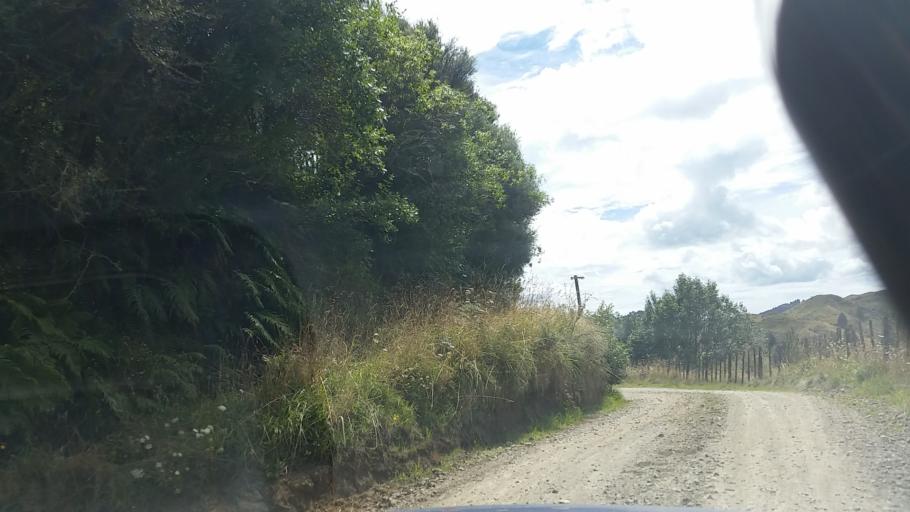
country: NZ
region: Taranaki
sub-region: South Taranaki District
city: Eltham
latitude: -39.2506
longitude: 174.5652
